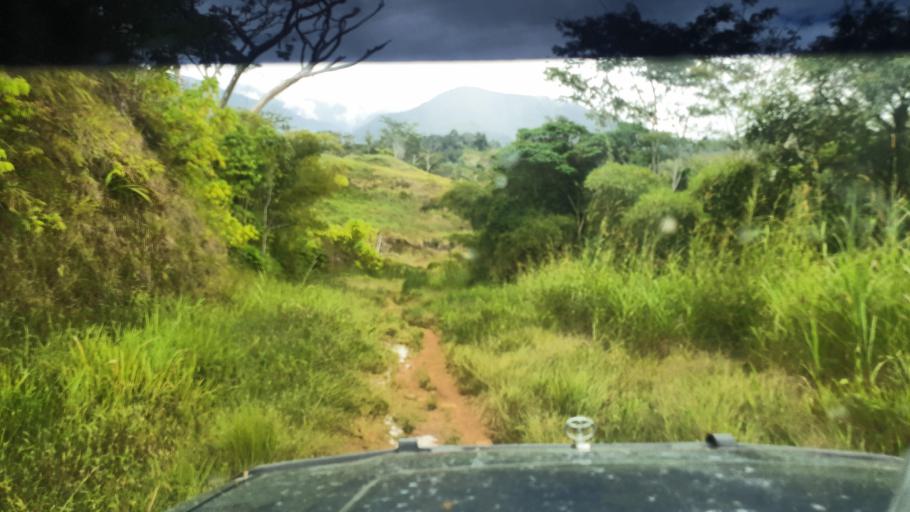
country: PG
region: Jiwaka
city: Minj
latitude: -5.8894
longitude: 144.8190
